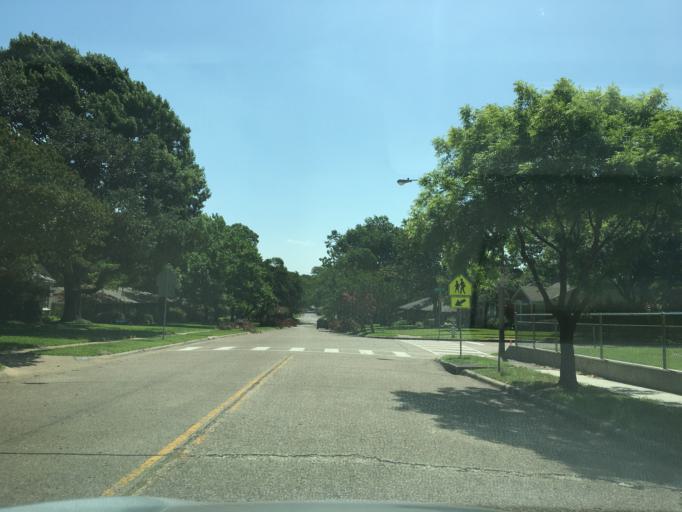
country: US
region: Texas
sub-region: Dallas County
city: University Park
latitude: 32.9031
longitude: -96.7838
